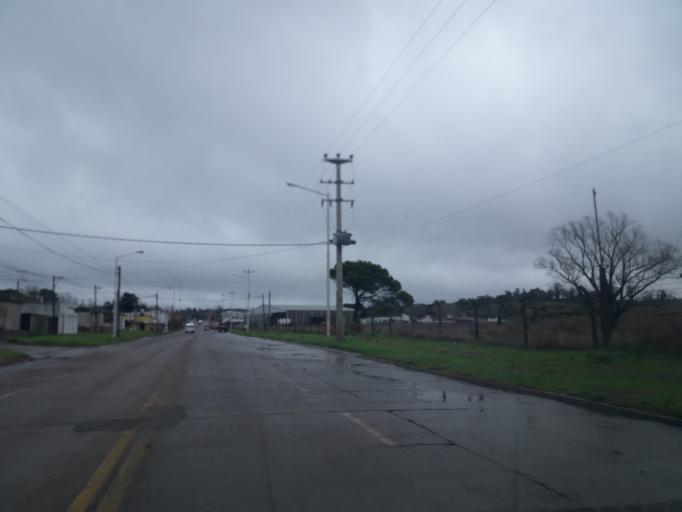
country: AR
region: Buenos Aires
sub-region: Partido de Tandil
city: Tandil
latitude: -37.3181
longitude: -59.1572
